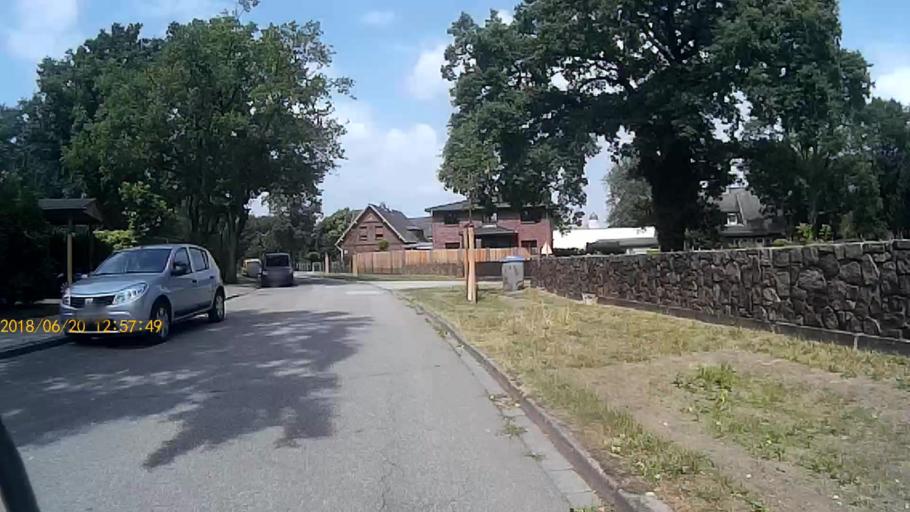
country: DE
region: Lower Saxony
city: Neu Wulmstorf
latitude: 53.4755
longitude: 9.8609
